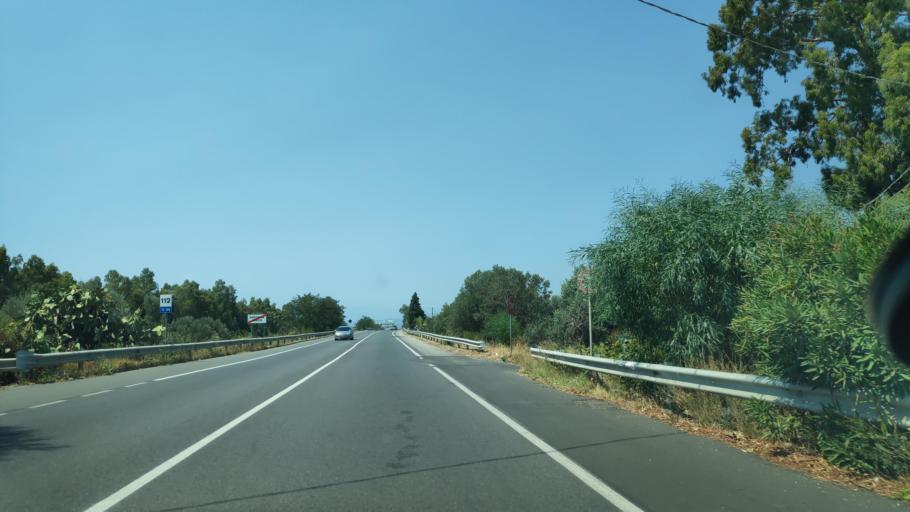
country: IT
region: Calabria
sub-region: Provincia di Reggio Calabria
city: Roccella Ionica
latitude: 38.3099
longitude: 16.3702
